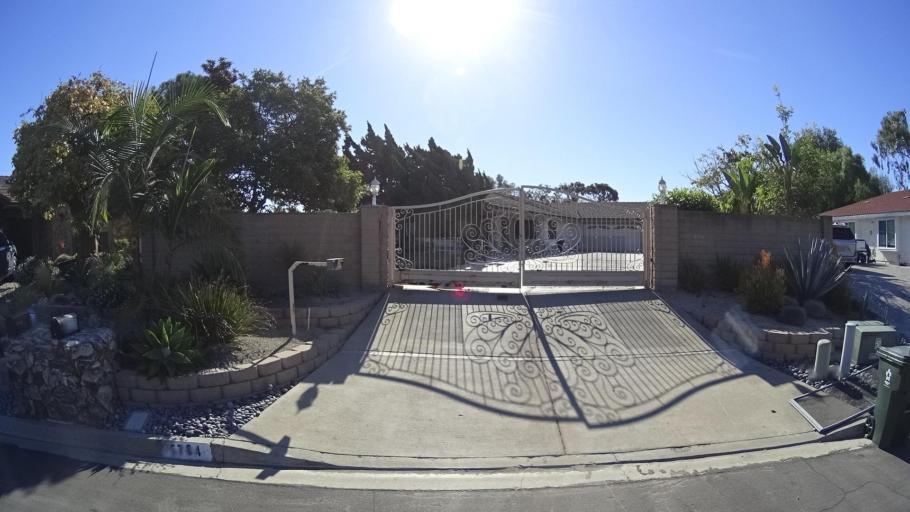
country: US
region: California
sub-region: San Diego County
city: Bonita
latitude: 32.6742
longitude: -117.0051
